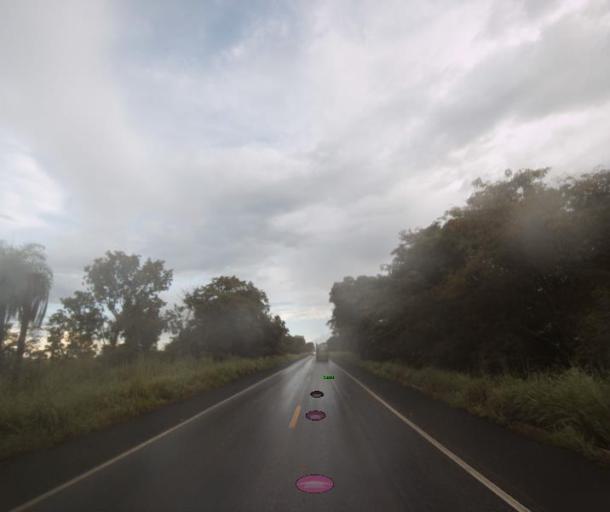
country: BR
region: Goias
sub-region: Porangatu
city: Porangatu
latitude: -13.8513
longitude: -49.0481
